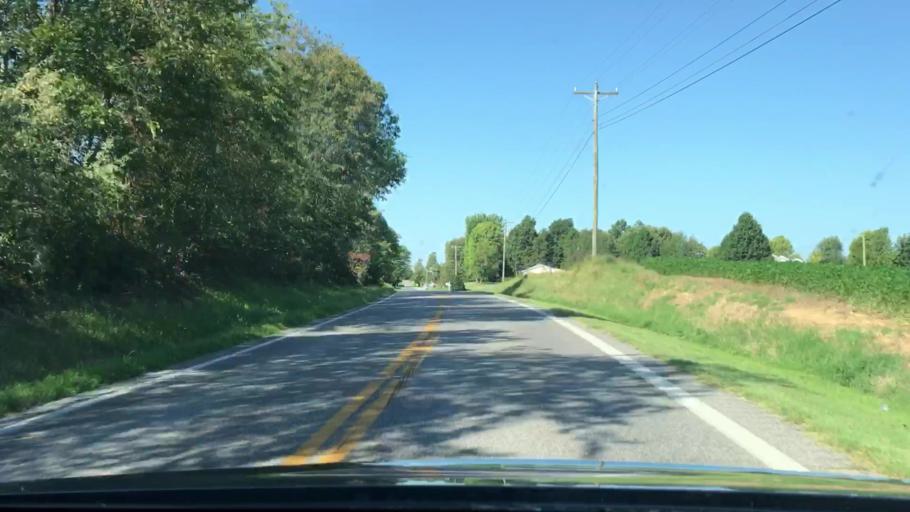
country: US
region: Kentucky
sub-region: Graves County
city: Mayfield
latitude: 36.7652
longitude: -88.5752
